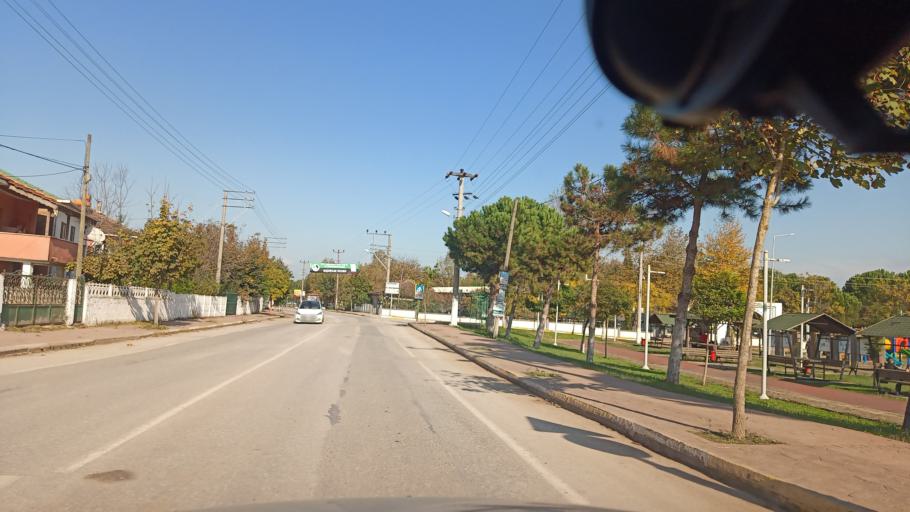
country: TR
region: Sakarya
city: Sogutlu
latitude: 40.8945
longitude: 30.4687
